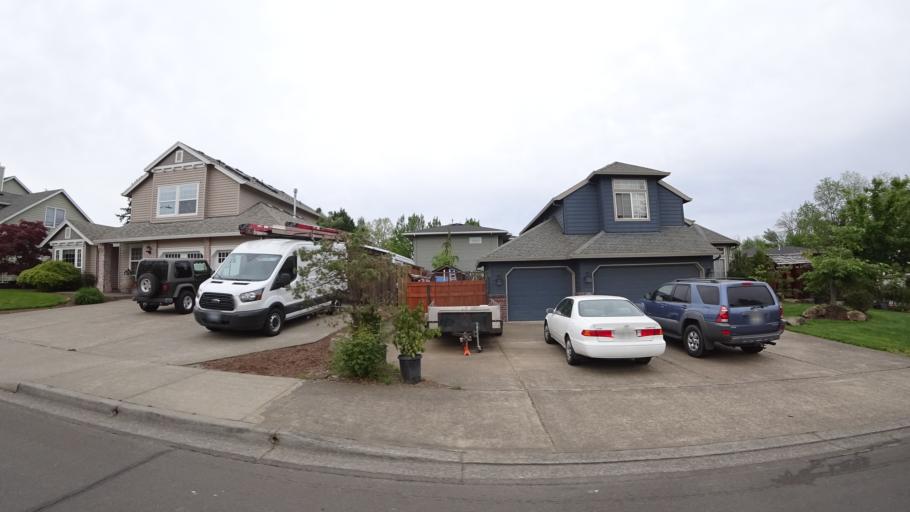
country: US
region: Oregon
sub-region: Washington County
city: Aloha
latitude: 45.5077
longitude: -122.9086
